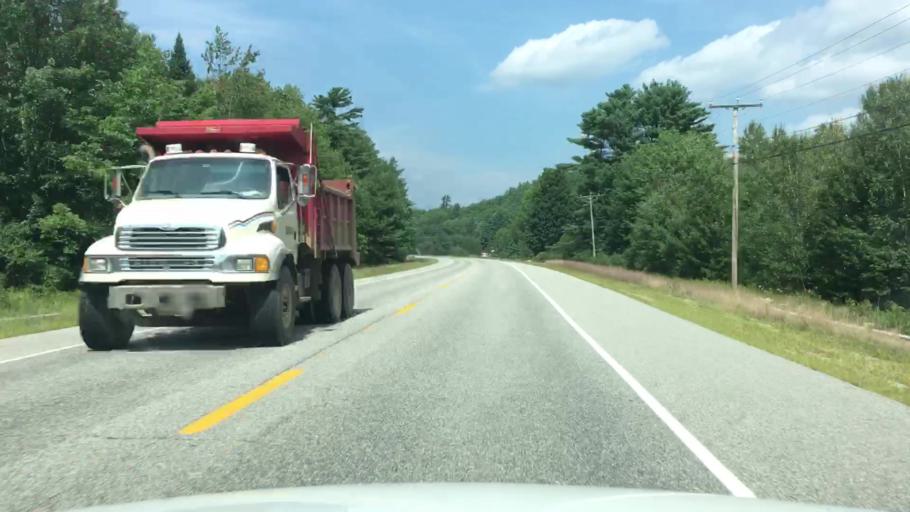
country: US
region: Maine
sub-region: Oxford County
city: Canton
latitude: 44.4511
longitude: -70.3173
